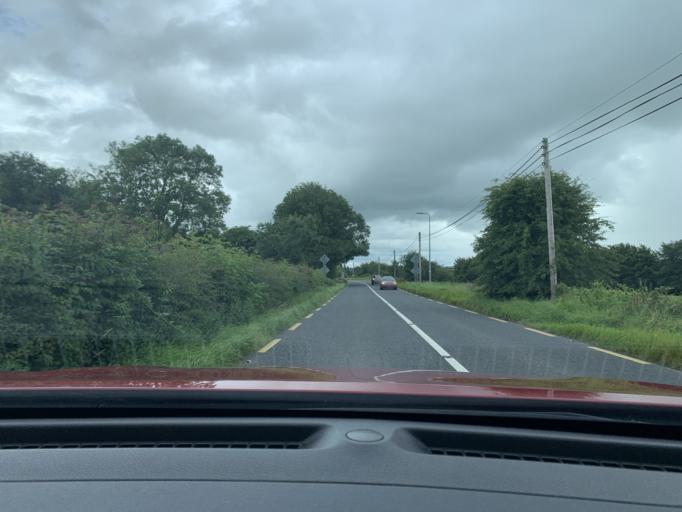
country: IE
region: Ulster
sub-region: County Donegal
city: Convoy
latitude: 54.8009
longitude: -7.6375
